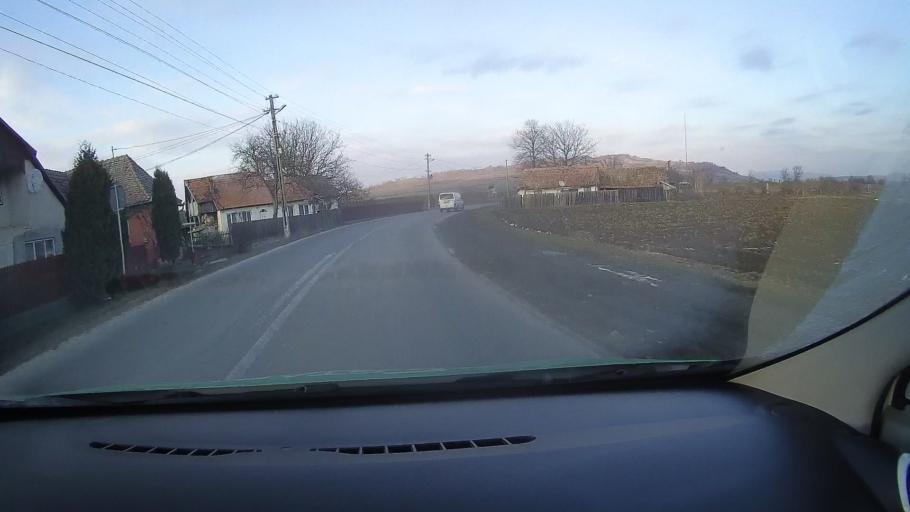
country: RO
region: Mures
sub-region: Comuna Vanatori
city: Vanatori
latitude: 46.2464
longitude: 24.9242
